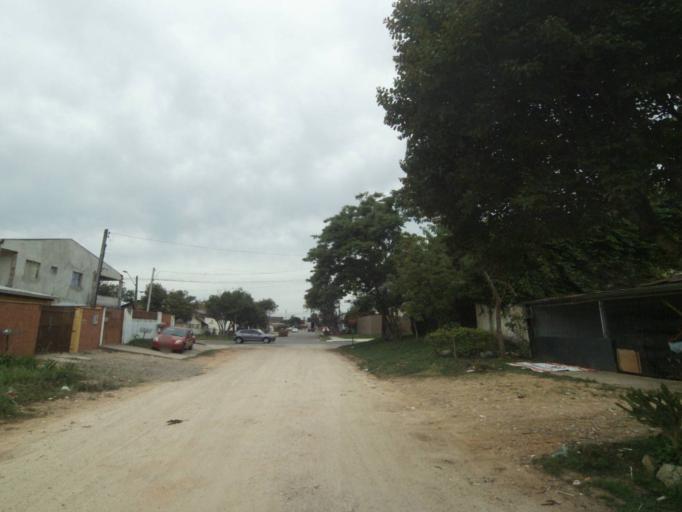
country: BR
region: Parana
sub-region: Pinhais
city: Pinhais
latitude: -25.4279
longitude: -49.2012
